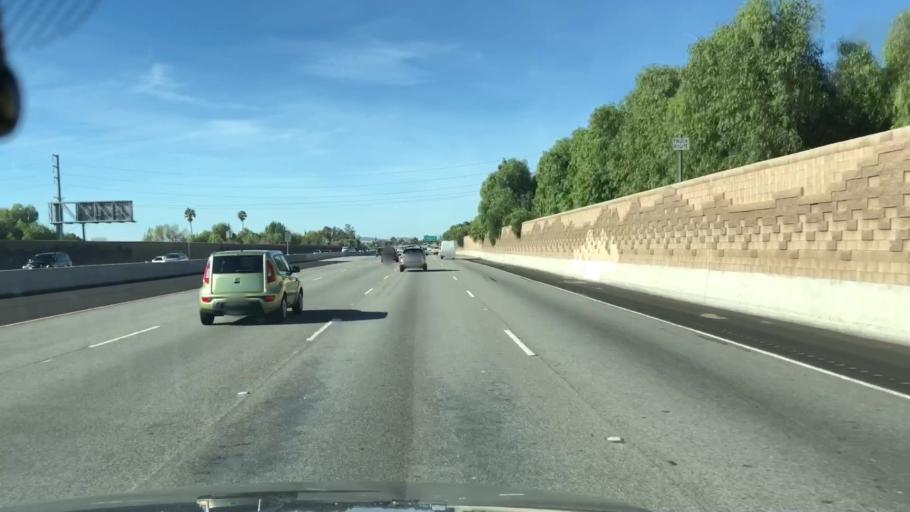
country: US
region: California
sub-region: Ventura County
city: Santa Susana
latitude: 34.2819
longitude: -118.7075
